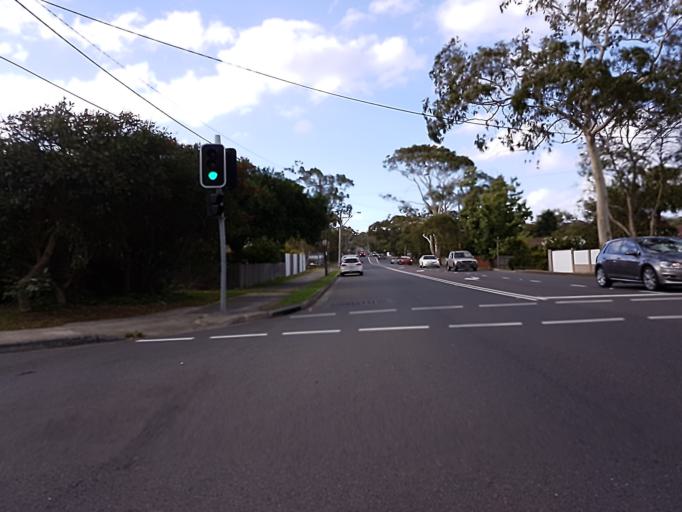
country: AU
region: New South Wales
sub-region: Manly Vale
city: Balgowlah
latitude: -33.7887
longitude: 151.2408
